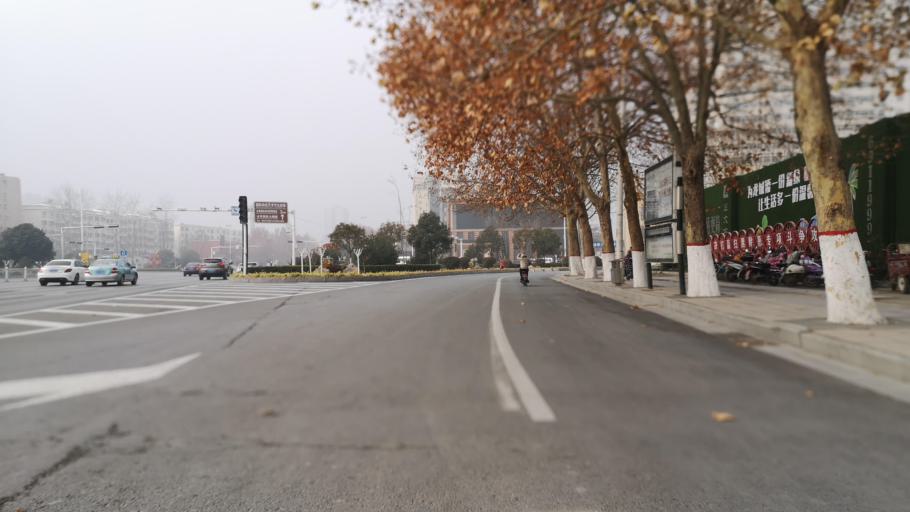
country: CN
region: Henan Sheng
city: Zhongyuanlu
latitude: 35.7806
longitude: 115.0455
